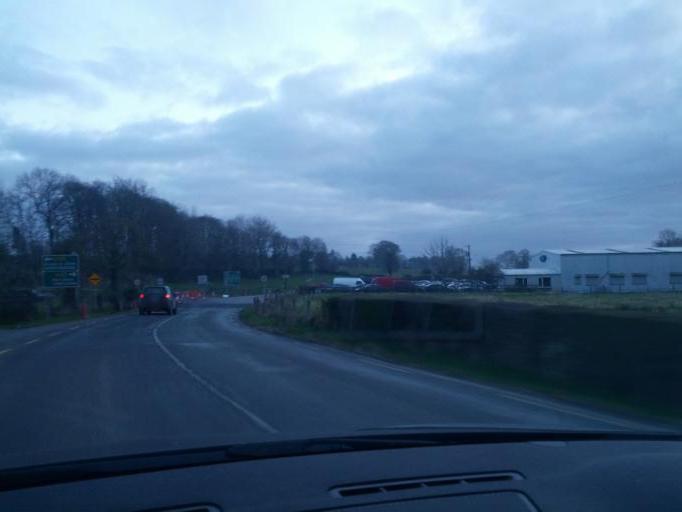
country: IE
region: Connaught
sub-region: County Galway
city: Portumna
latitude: 53.0912
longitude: -8.1847
